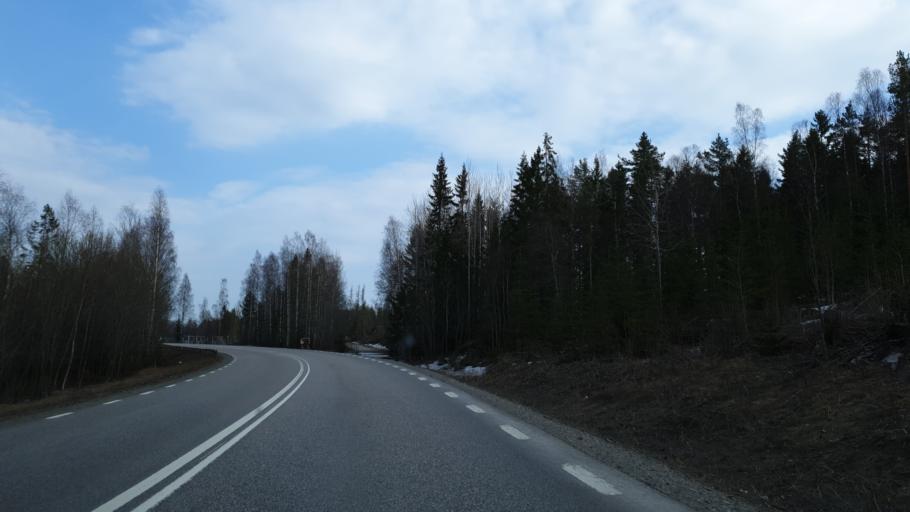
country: SE
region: Gaevleborg
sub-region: Hudiksvalls Kommun
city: Iggesund
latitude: 61.6511
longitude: 17.0308
